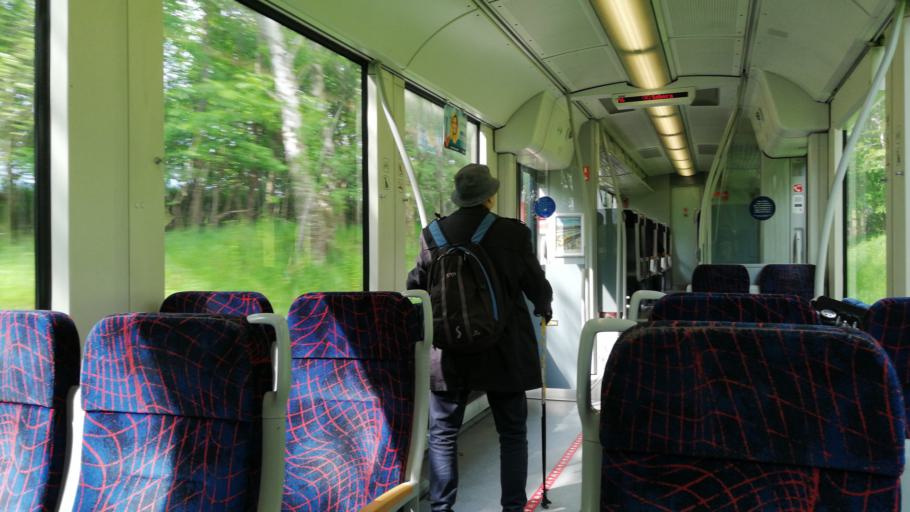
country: DK
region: Capital Region
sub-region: Gribskov Kommune
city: Gilleleje
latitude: 56.0982
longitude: 12.3498
